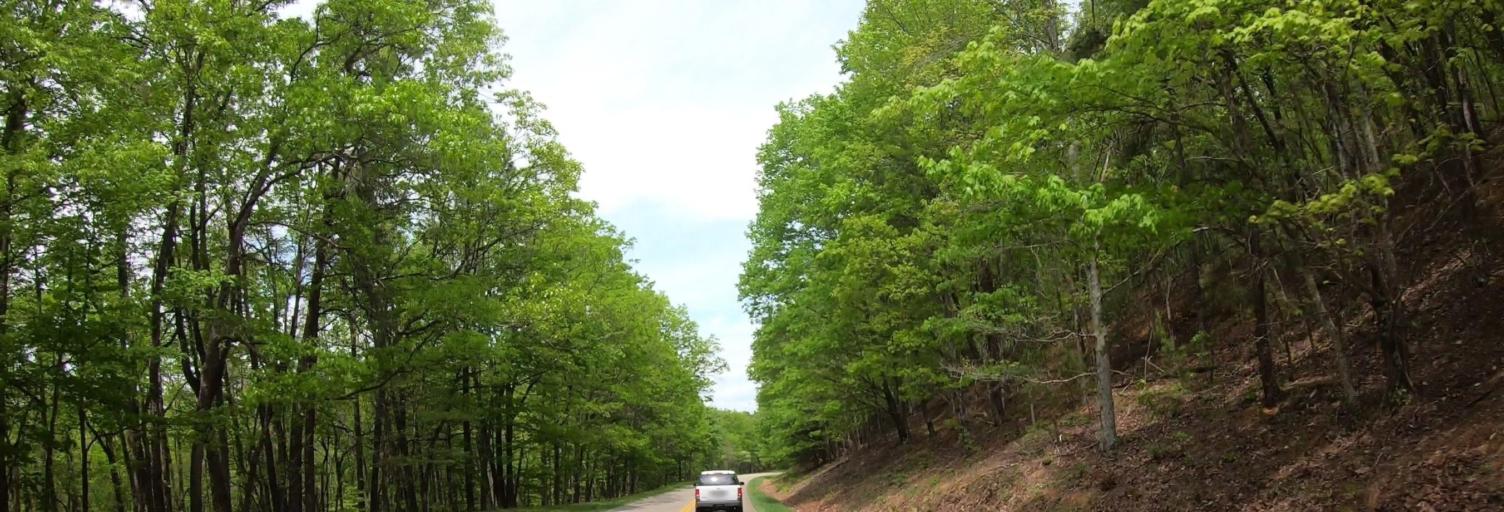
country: US
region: Virginia
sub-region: Roanoke County
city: Narrows
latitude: 37.2209
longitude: -79.9438
